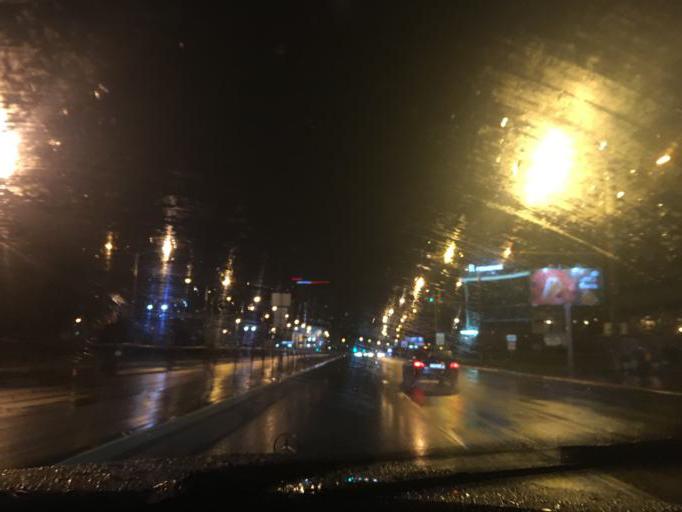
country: BY
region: Minsk
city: Minsk
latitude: 53.8911
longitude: 27.5251
